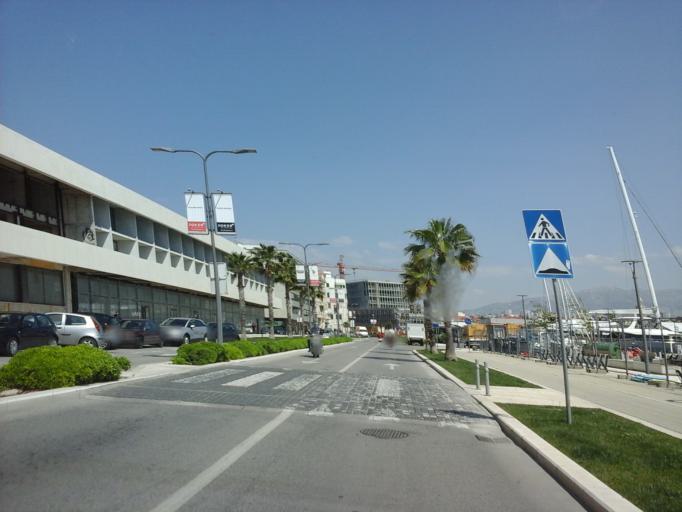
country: HR
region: Splitsko-Dalmatinska
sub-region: Grad Split
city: Split
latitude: 43.5052
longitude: 16.4306
